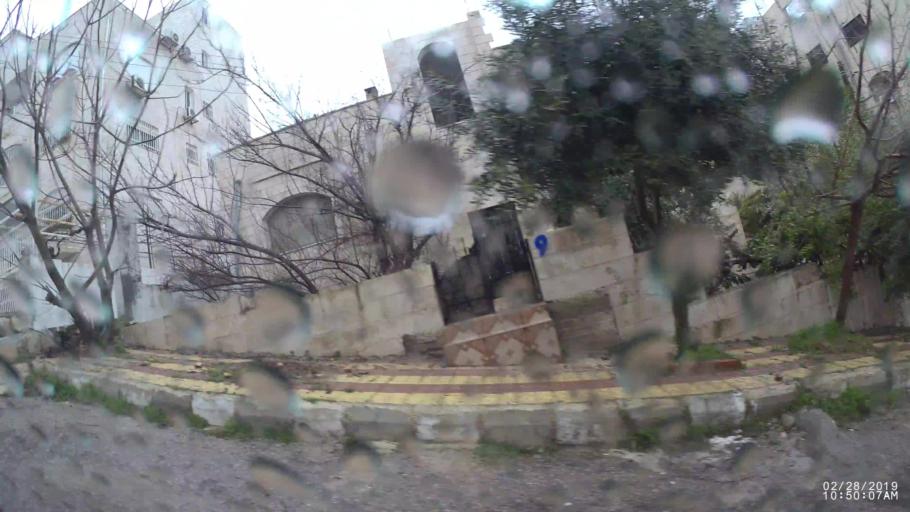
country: JO
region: Amman
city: Al Jubayhah
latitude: 32.0123
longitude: 35.8918
